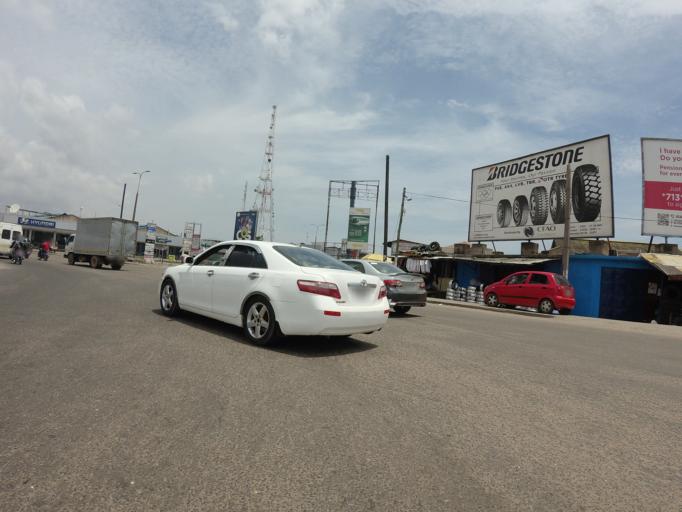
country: GH
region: Greater Accra
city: Accra
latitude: 5.5610
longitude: -0.2293
